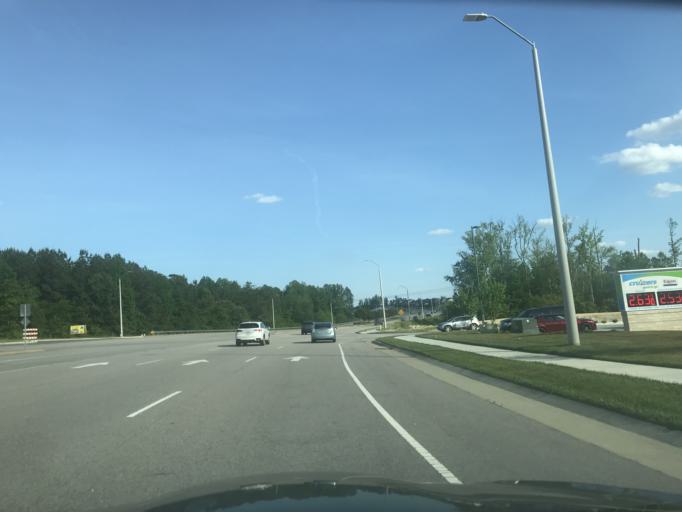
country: US
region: North Carolina
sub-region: Wake County
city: Knightdale
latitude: 35.7804
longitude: -78.4363
